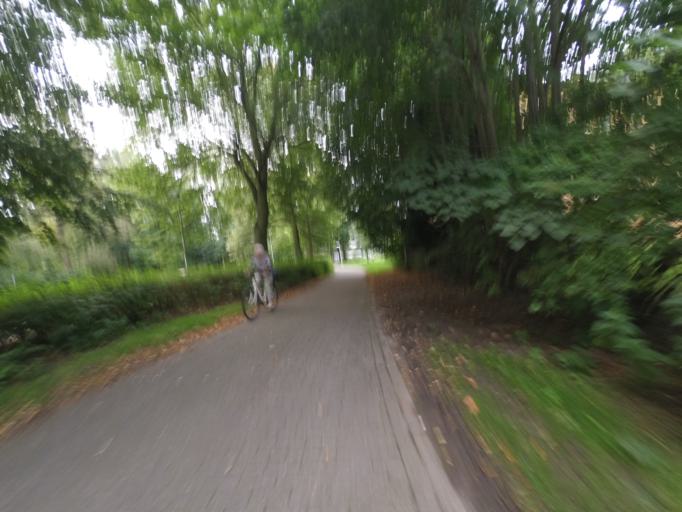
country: DE
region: Hamburg
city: Wandsbek
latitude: 53.5423
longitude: 10.1182
